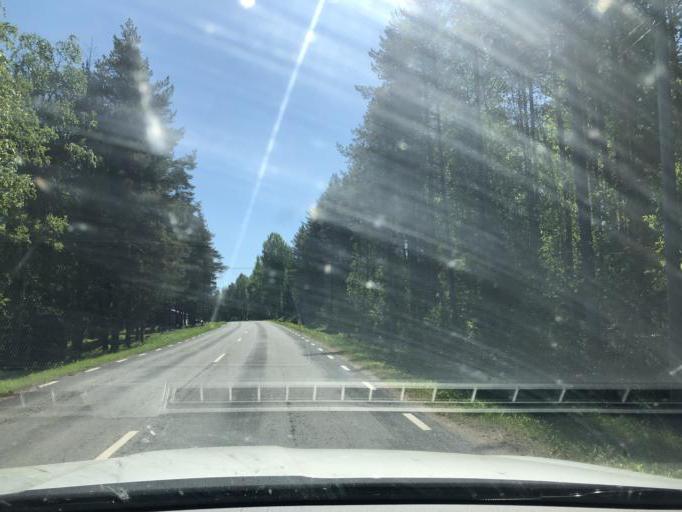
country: SE
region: Norrbotten
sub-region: Lulea Kommun
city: Sodra Sunderbyn
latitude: 65.6625
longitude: 21.9744
